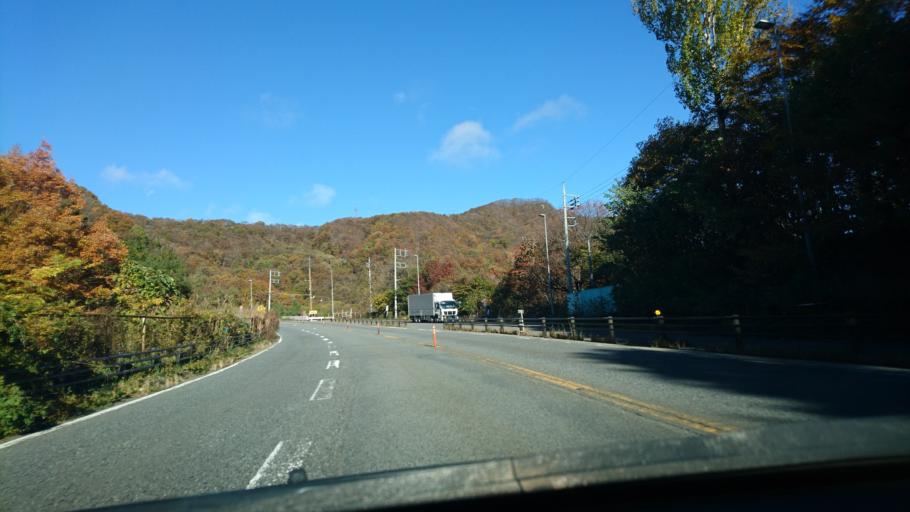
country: JP
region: Nagano
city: Saku
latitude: 36.3161
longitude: 138.6562
